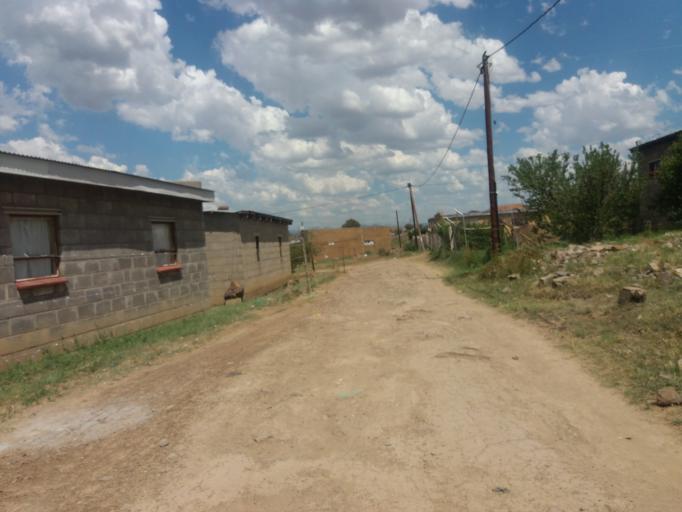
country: LS
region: Maseru
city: Maseru
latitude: -29.3652
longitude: 27.4752
